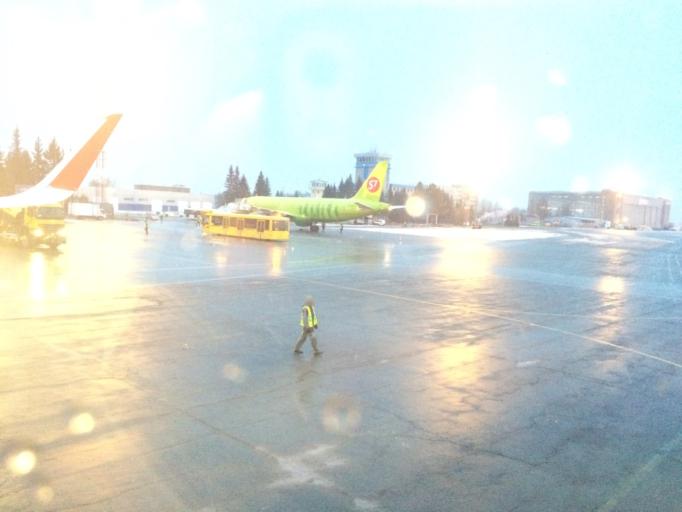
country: RU
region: Novosibirsk
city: Ob'
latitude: 55.0107
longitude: 82.6660
